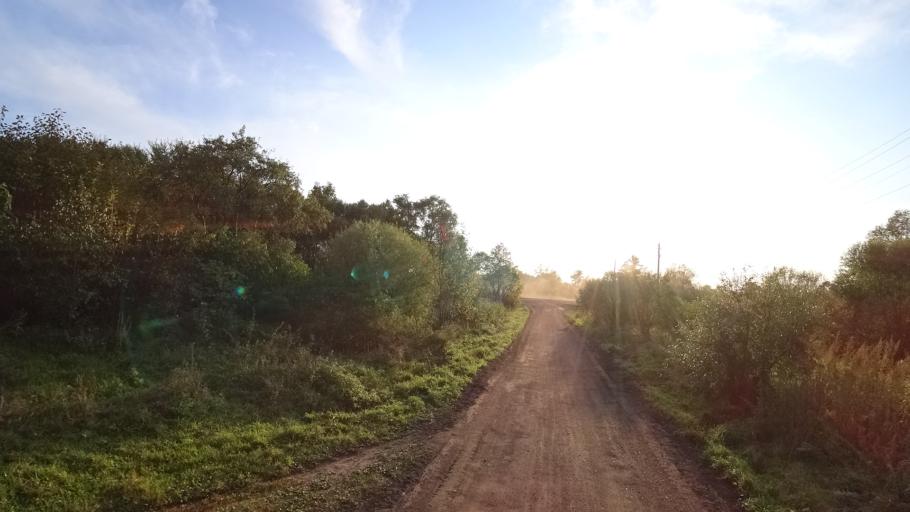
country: RU
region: Amur
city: Arkhara
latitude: 49.3546
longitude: 130.1108
